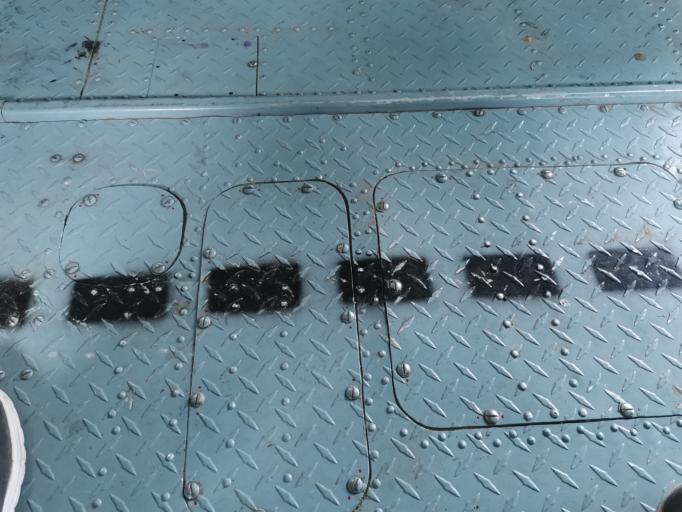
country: RU
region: Sverdlovsk
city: Sos'va
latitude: 59.1850
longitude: 61.8287
